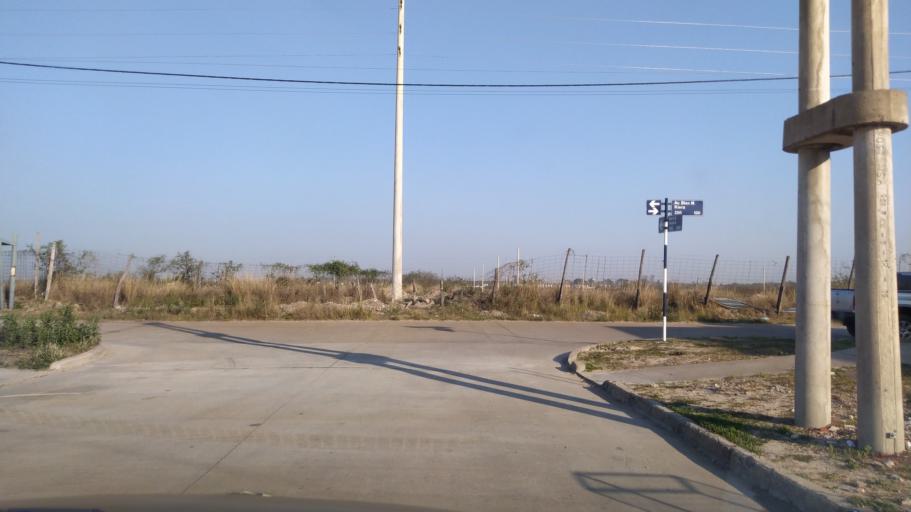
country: AR
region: Corrientes
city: Corrientes
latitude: -27.5250
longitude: -58.8076
